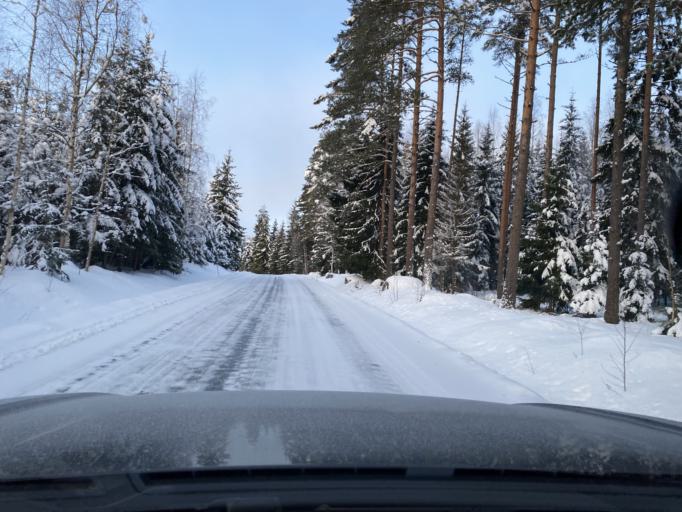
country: FI
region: Haeme
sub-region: Forssa
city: Tammela
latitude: 60.8632
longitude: 23.8876
